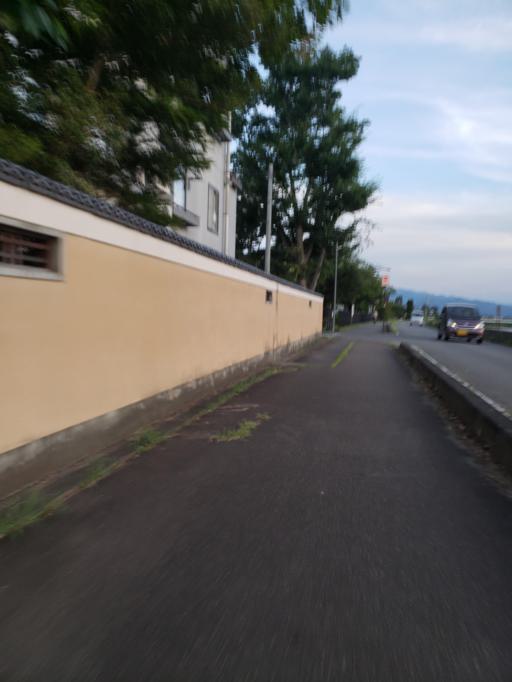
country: JP
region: Nagano
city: Nagano-shi
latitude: 36.6371
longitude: 138.1799
